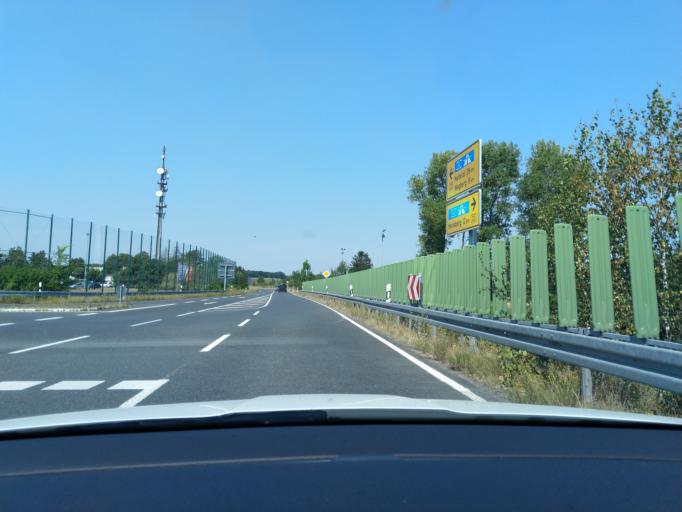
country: DE
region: North Rhine-Westphalia
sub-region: Regierungsbezirk Koln
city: Wassenberg
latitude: 51.1197
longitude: 6.2027
